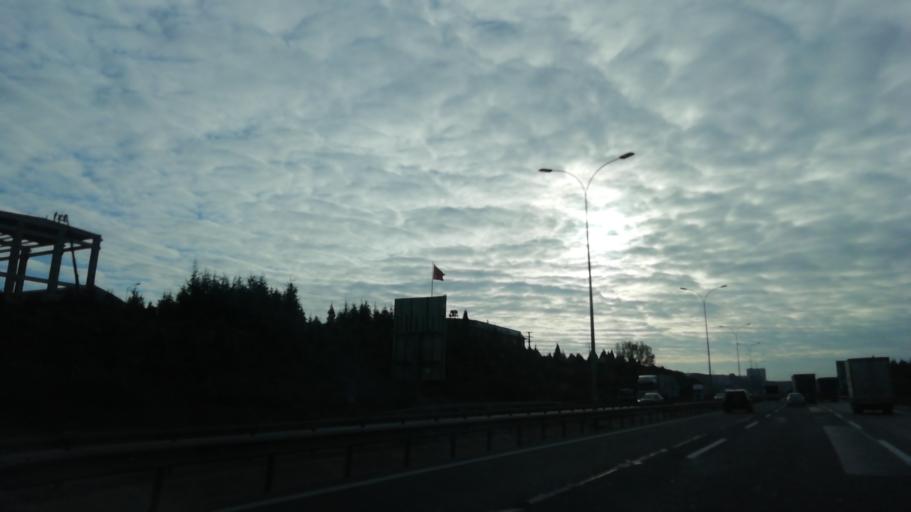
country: TR
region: Kocaeli
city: Balcik
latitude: 40.8629
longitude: 29.4013
